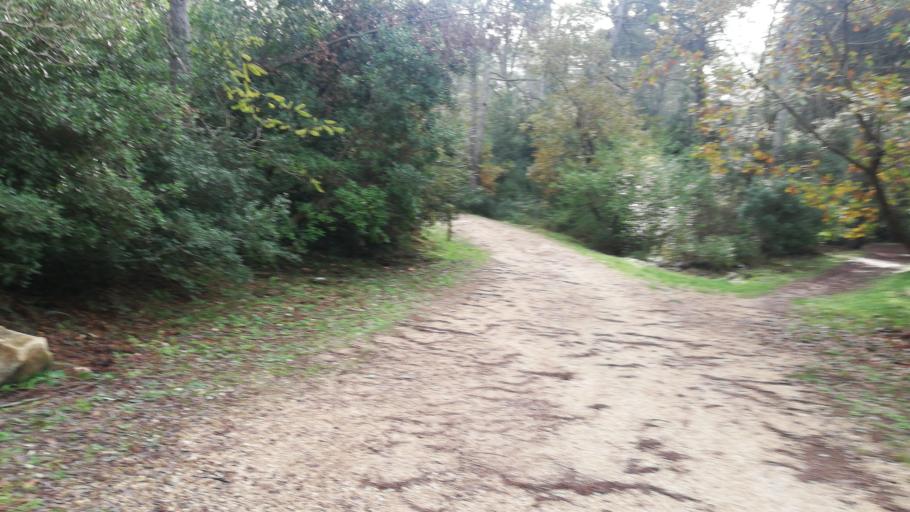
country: IT
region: Apulia
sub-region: Provincia di Bari
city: Cassano delle Murge
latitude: 40.8839
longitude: 16.7038
